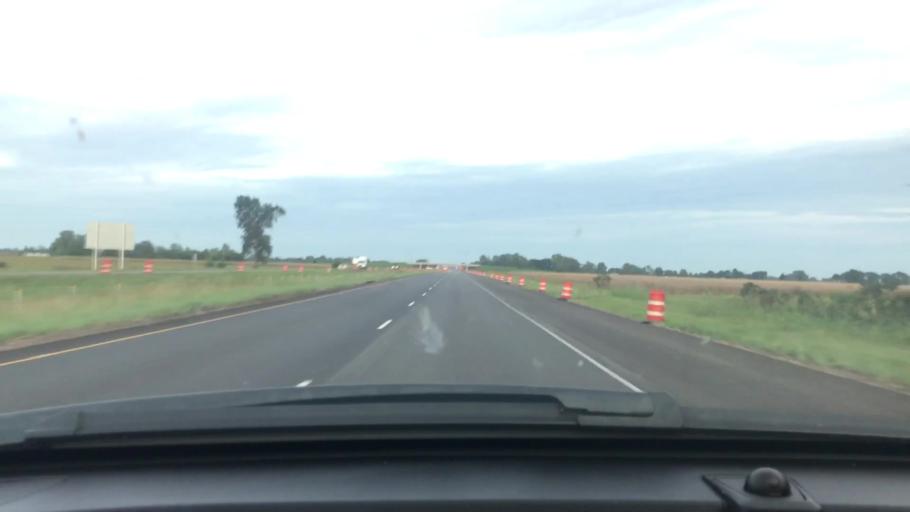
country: US
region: Arkansas
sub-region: Poinsett County
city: Trumann
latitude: 35.6580
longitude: -90.5442
